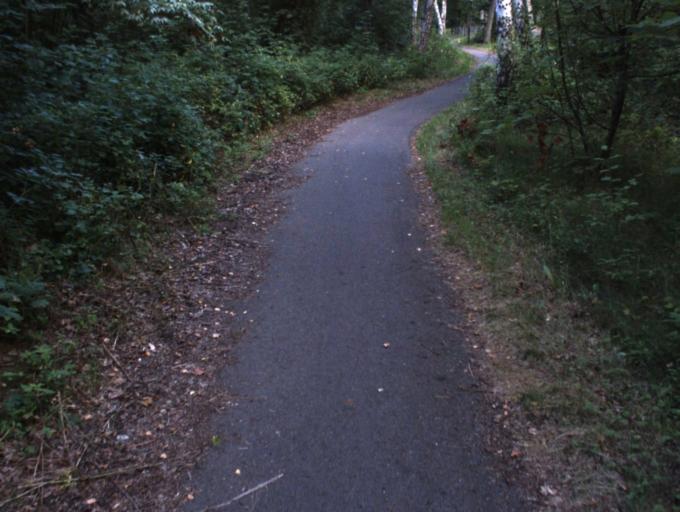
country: DK
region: Capital Region
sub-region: Helsingor Kommune
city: Helsingor
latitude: 56.1118
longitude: 12.6203
